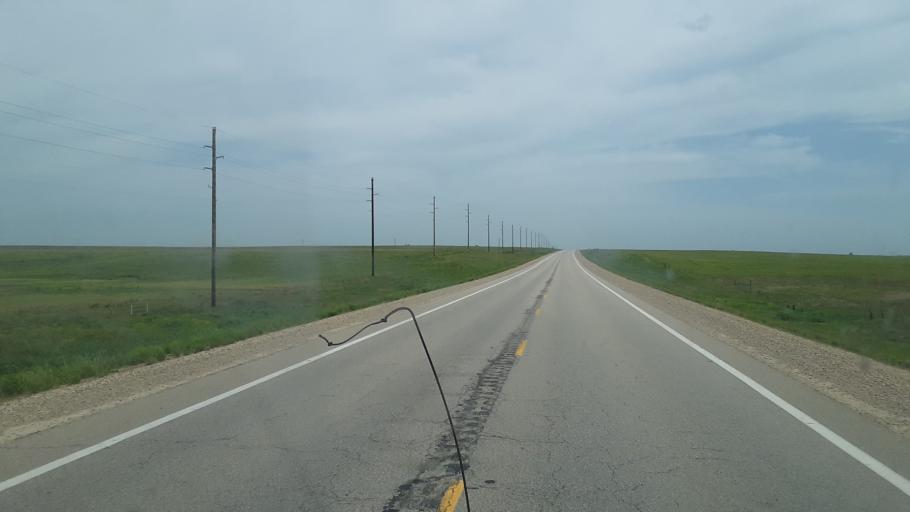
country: US
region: Kansas
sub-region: Greenwood County
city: Eureka
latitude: 37.8381
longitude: -96.1378
